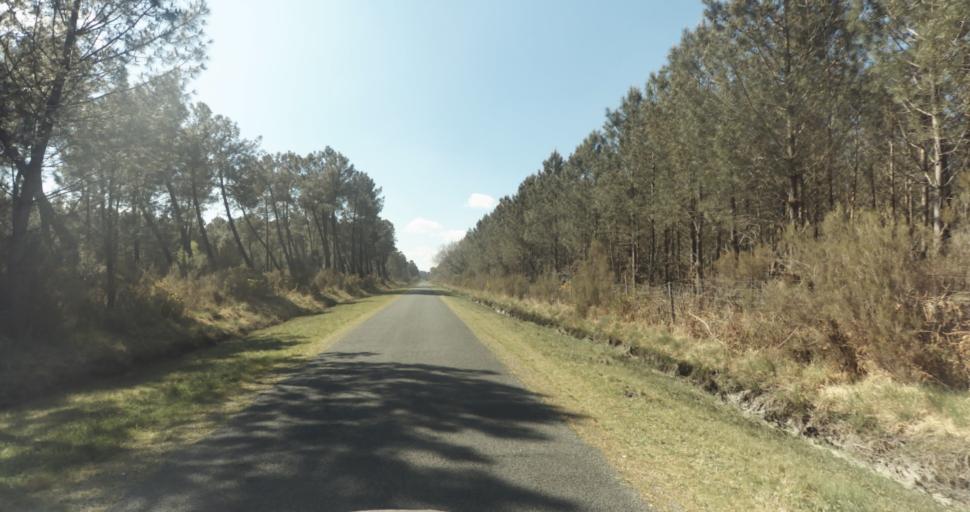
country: FR
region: Aquitaine
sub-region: Departement de la Gironde
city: Martignas-sur-Jalle
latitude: 44.7790
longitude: -0.8033
